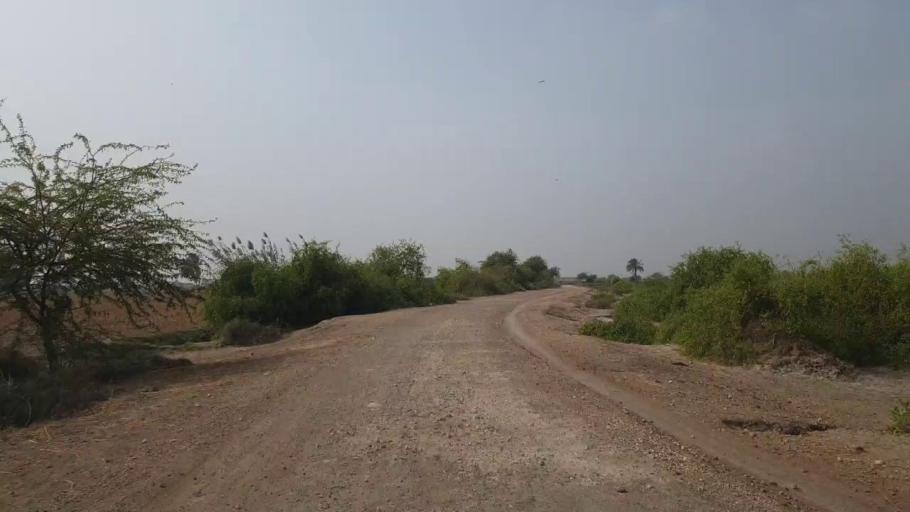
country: PK
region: Sindh
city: Kario
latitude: 24.8778
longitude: 68.5090
